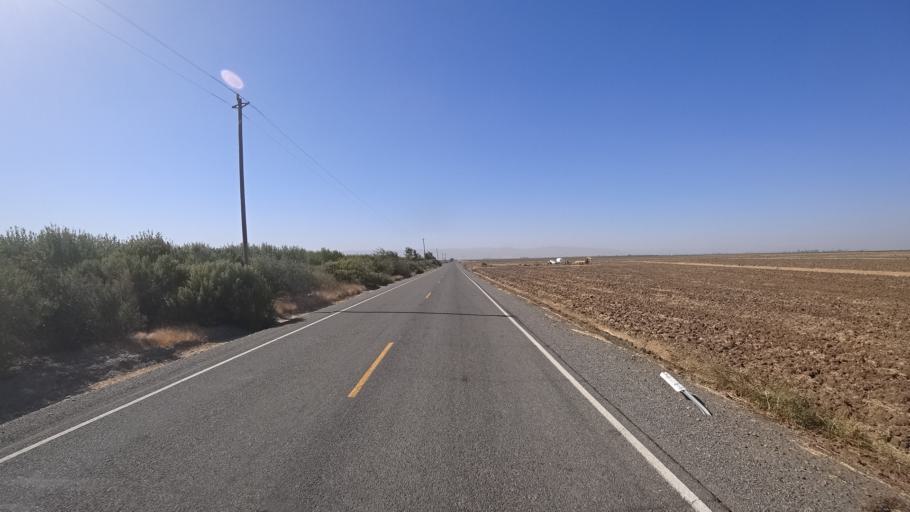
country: US
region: California
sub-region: Yolo County
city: Winters
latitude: 38.5907
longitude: -121.8901
